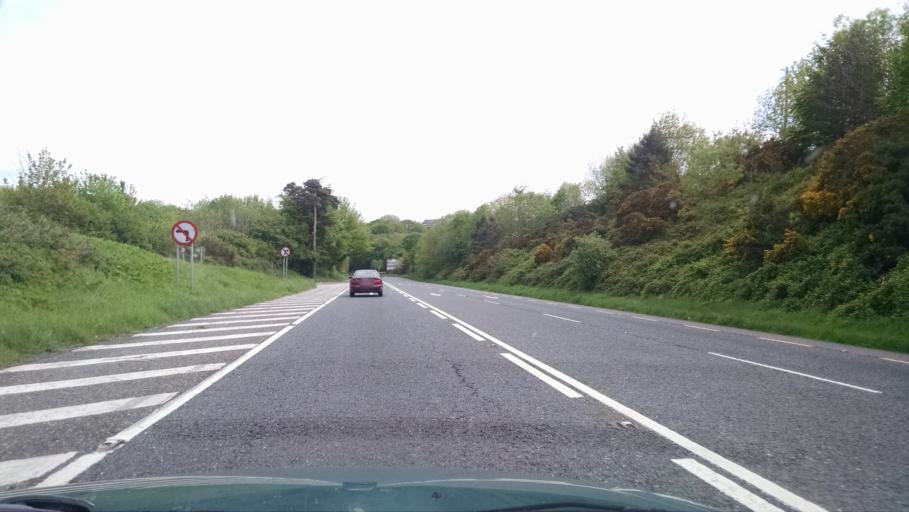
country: IE
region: Munster
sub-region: County Cork
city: Carrigaline
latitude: 51.8670
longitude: -8.4150
